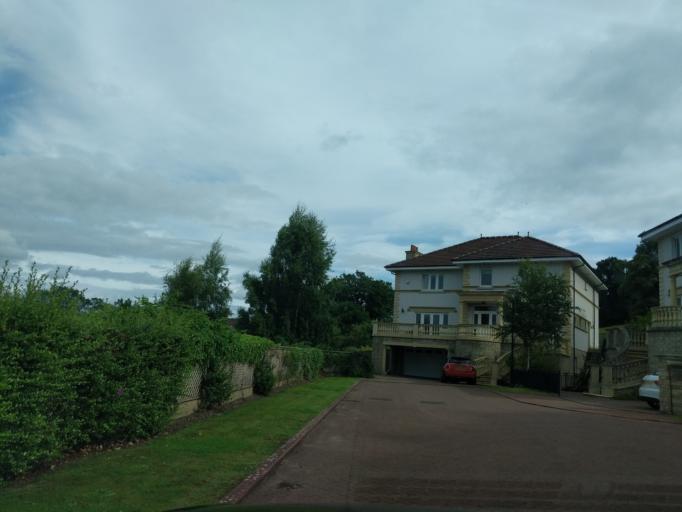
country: GB
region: Scotland
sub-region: Edinburgh
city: Colinton
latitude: 55.9564
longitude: -3.2703
